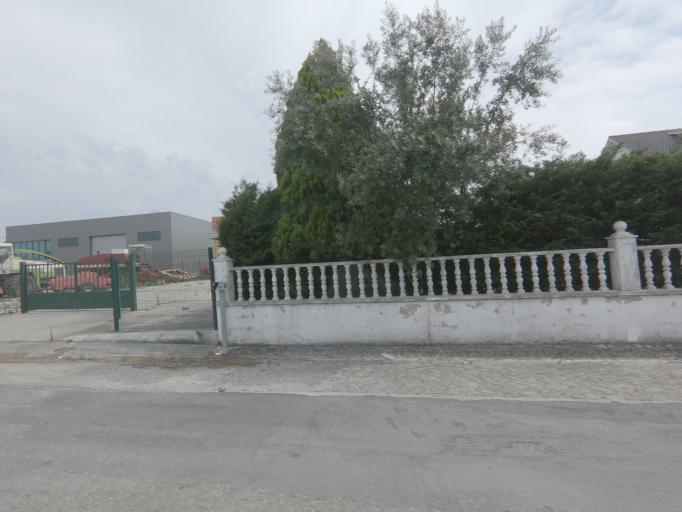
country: PT
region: Leiria
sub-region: Pombal
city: Pombal
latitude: 39.8762
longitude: -8.6840
